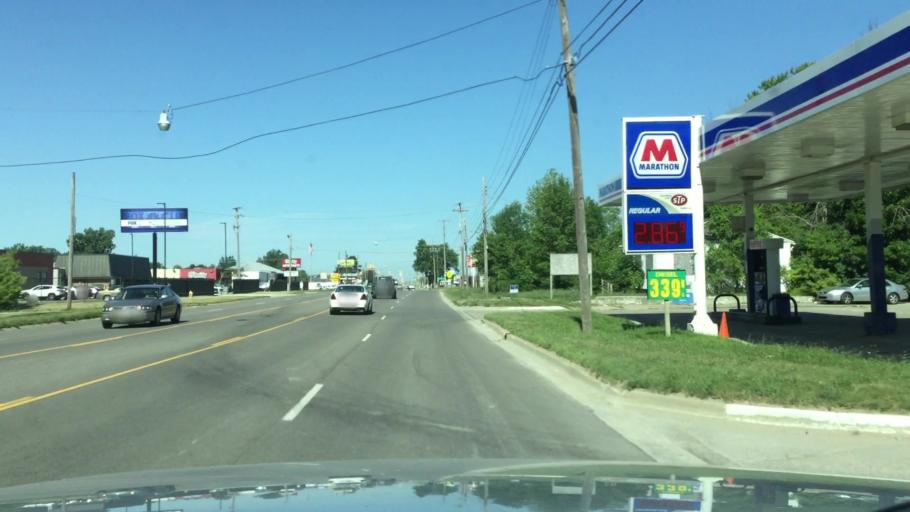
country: US
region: Michigan
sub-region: Genesee County
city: Beecher
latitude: 43.0608
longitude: -83.7489
